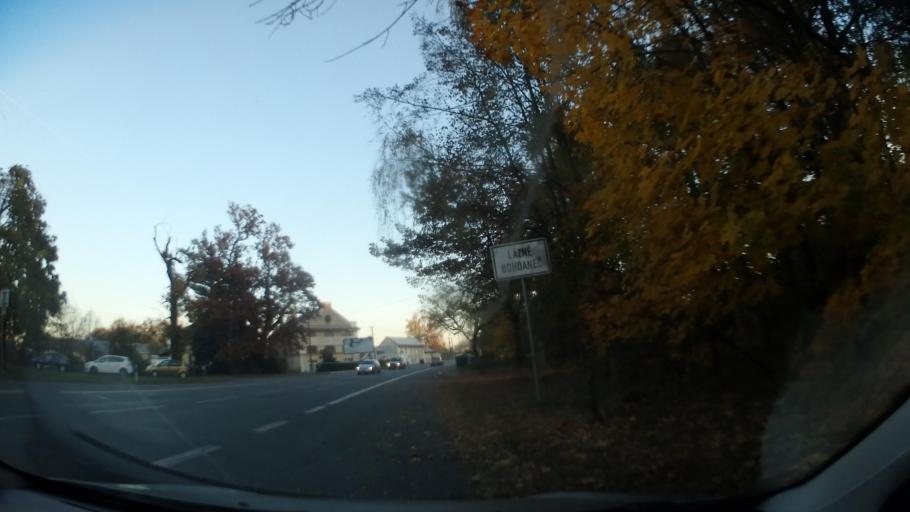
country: CZ
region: Pardubicky
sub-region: Okres Pardubice
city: Lazne Bohdanec
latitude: 50.0856
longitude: 15.6676
